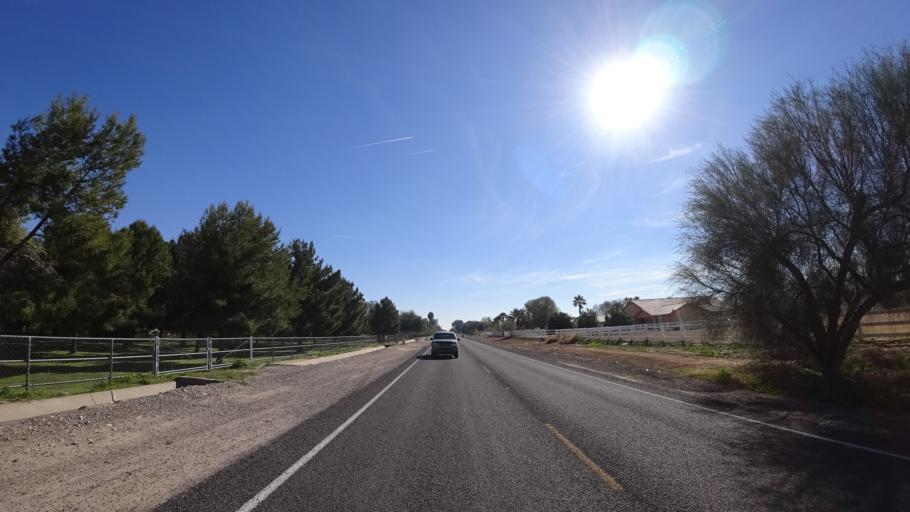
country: US
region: Arizona
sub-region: Maricopa County
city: Citrus Park
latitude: 33.5477
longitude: -112.4442
